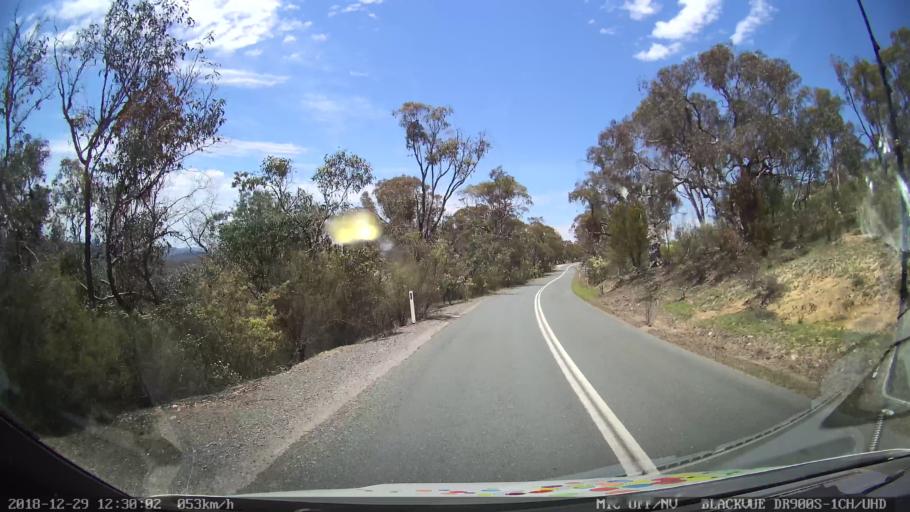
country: AU
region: Australian Capital Territory
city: Macarthur
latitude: -35.5027
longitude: 149.2327
